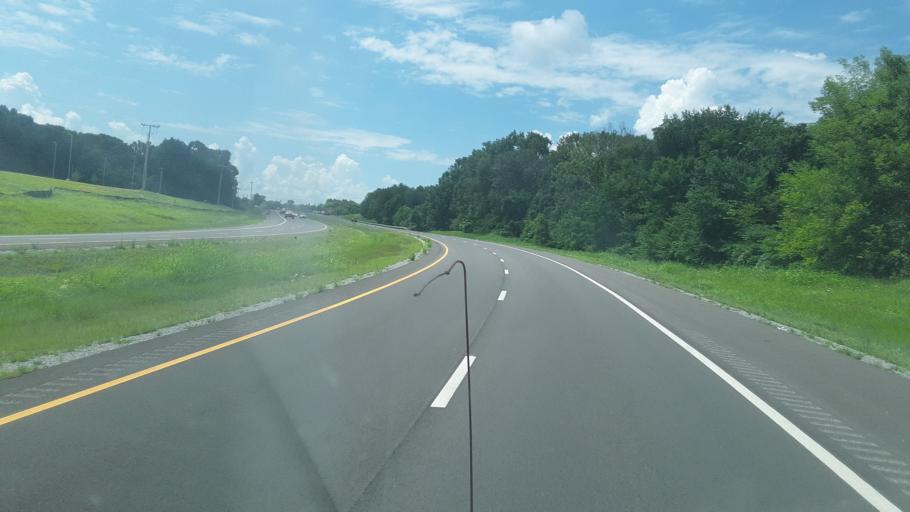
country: US
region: Kentucky
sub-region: Christian County
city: Fort Campbell North
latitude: 36.5809
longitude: -87.4442
